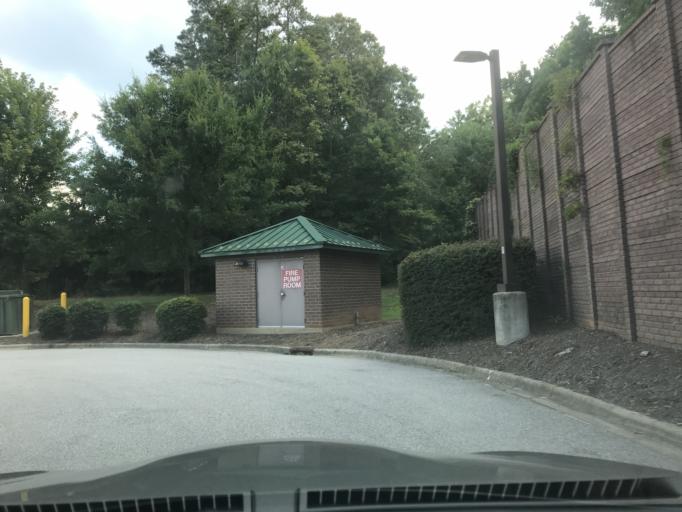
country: US
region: North Carolina
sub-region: Wake County
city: Wake Forest
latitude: 35.9076
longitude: -78.6022
